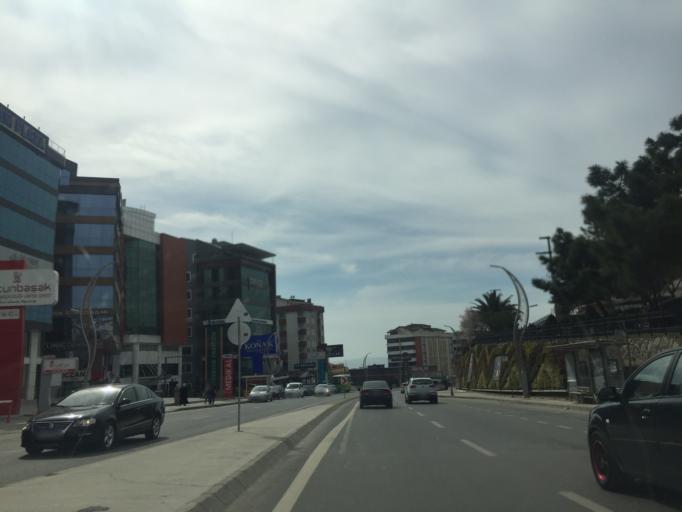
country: TR
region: Kocaeli
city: Gebze
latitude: 40.7899
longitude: 29.4205
